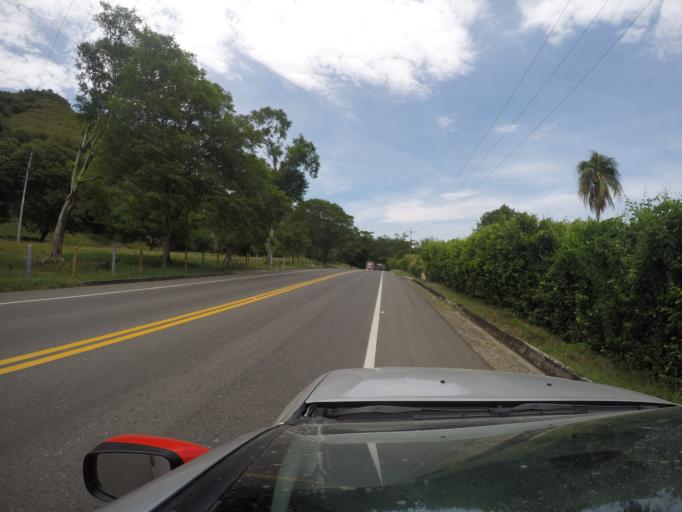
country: CO
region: Tolima
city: Honda
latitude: 5.2509
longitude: -74.7285
